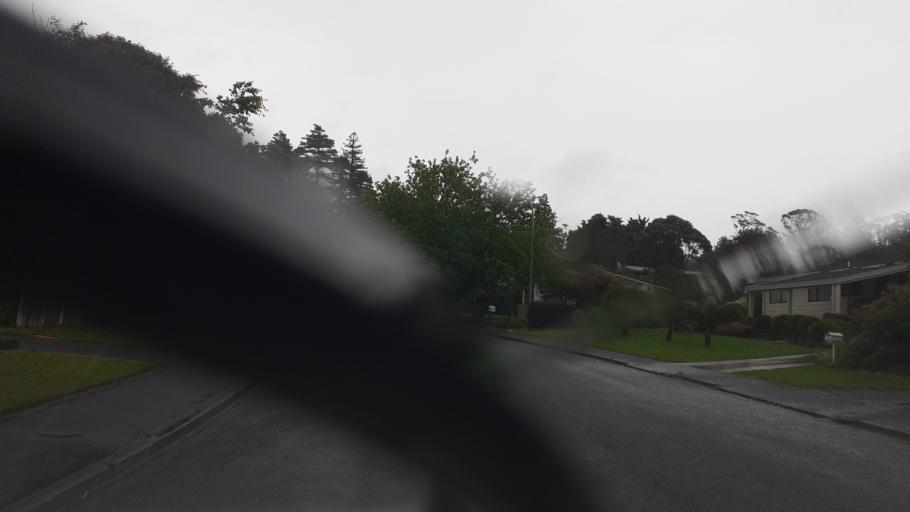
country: NZ
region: Northland
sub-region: Far North District
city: Kerikeri
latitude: -35.2234
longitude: 173.9551
